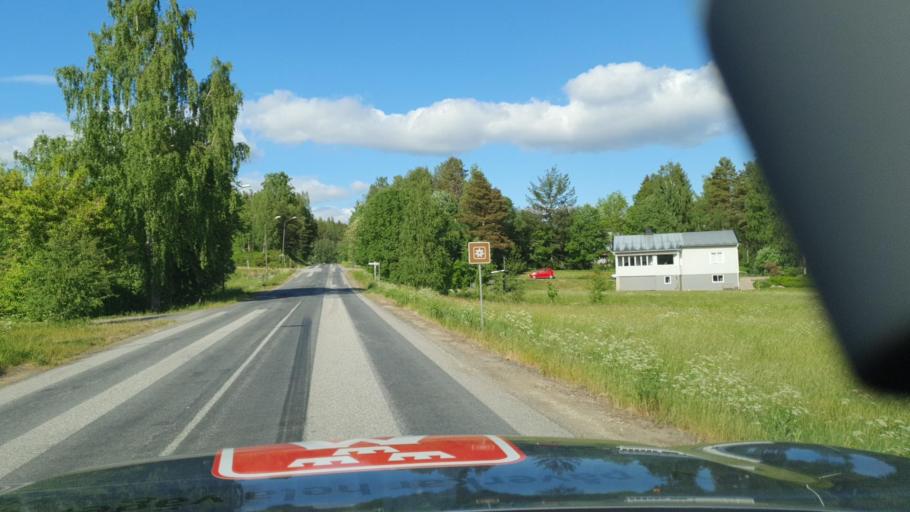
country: SE
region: Vaesternorrland
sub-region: Haernoesands Kommun
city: Haernoesand
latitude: 62.8164
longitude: 17.9528
